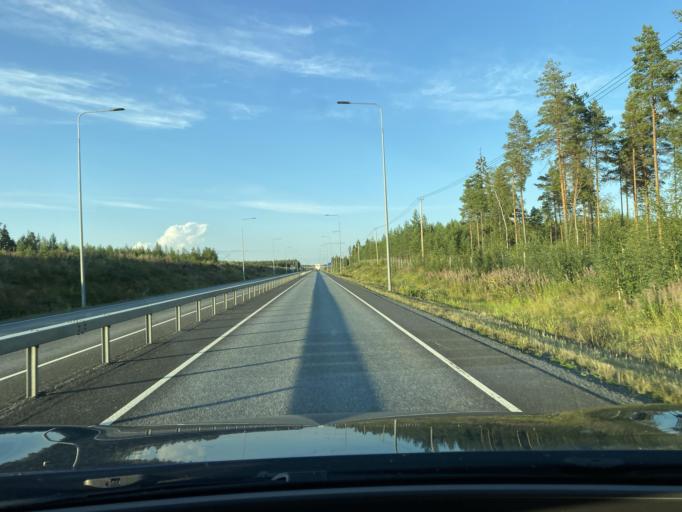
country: FI
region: Southern Ostrobothnia
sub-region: Seinaejoki
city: Seinaejoki
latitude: 62.7158
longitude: 22.8560
